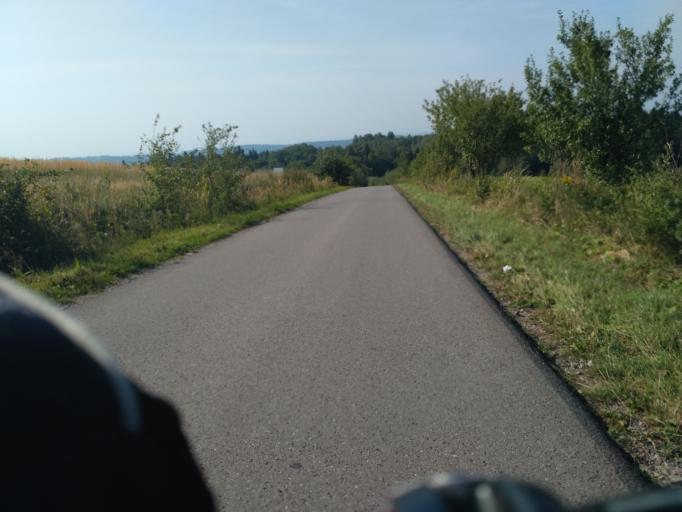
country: PL
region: Subcarpathian Voivodeship
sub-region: Powiat brzozowski
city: Golcowa
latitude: 49.7979
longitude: 22.0257
